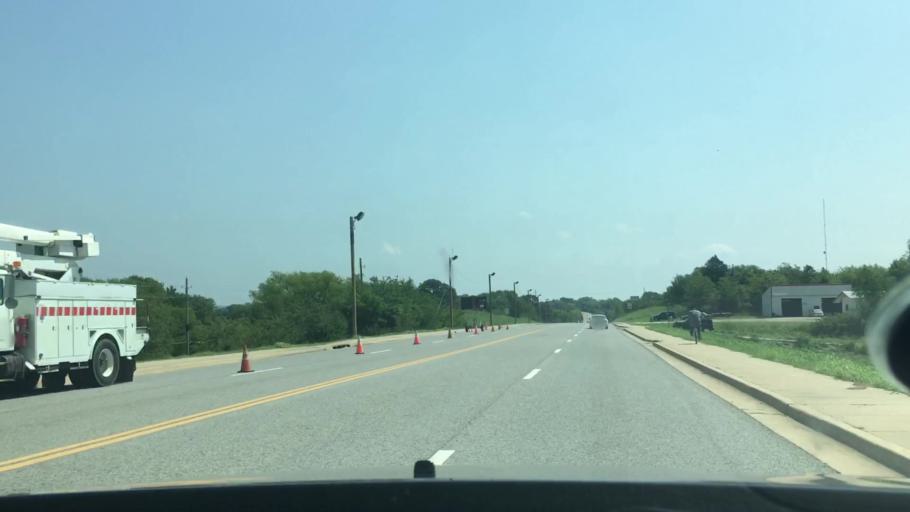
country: US
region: Oklahoma
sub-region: Atoka County
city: Atoka
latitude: 34.3747
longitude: -96.1248
